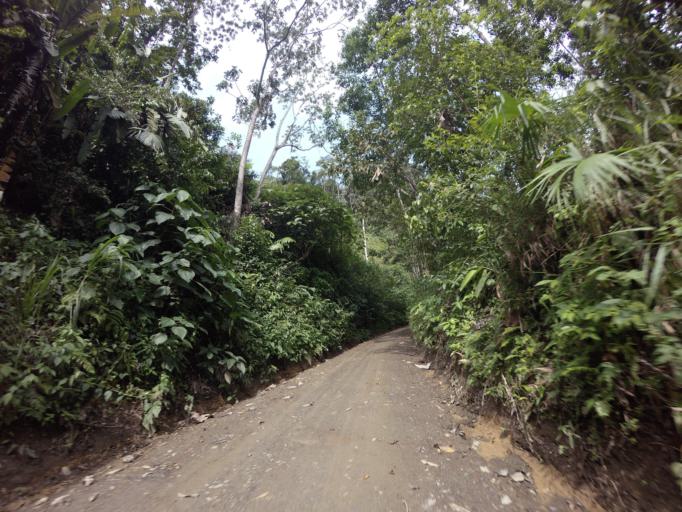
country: CO
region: Caldas
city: Marquetalia
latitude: 5.3347
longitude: -75.0522
